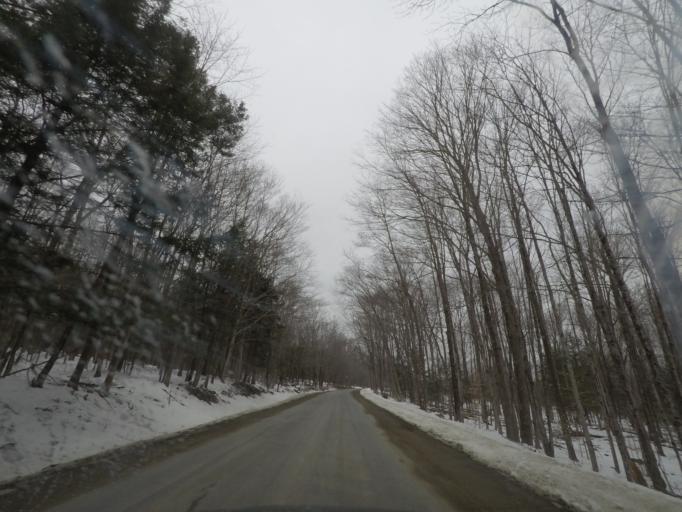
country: US
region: New York
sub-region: Rensselaer County
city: Averill Park
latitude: 42.5541
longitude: -73.4134
